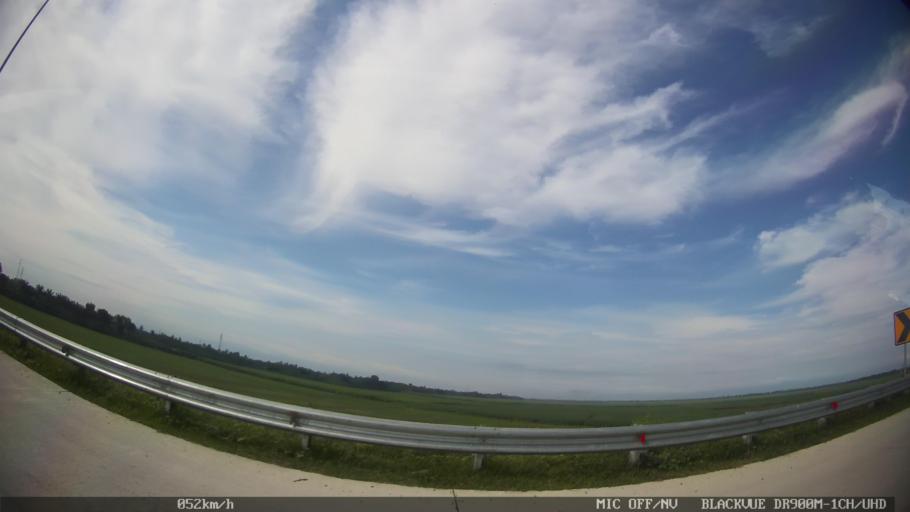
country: ID
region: North Sumatra
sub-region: Kabupaten Langkat
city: Stabat
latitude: 3.7122
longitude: 98.4938
